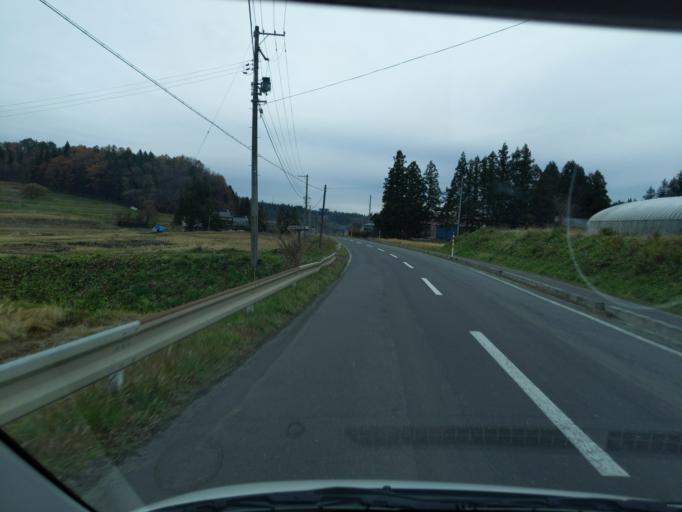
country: JP
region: Iwate
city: Kitakami
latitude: 39.2711
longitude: 141.2677
